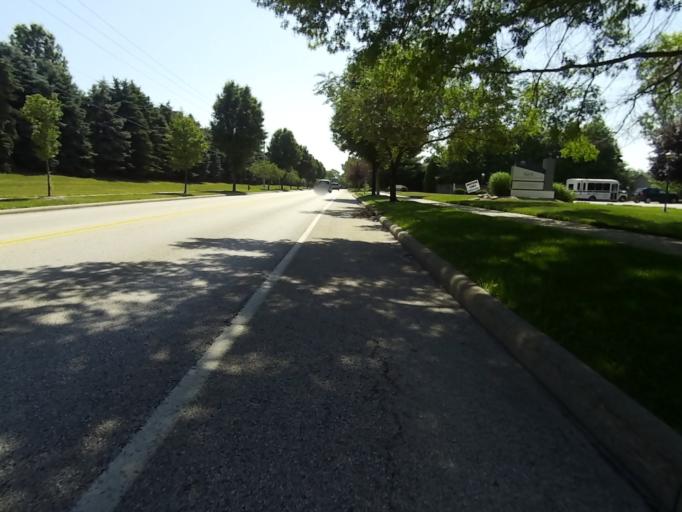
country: US
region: Ohio
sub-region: Portage County
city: Kent
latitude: 41.1647
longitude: -81.3846
